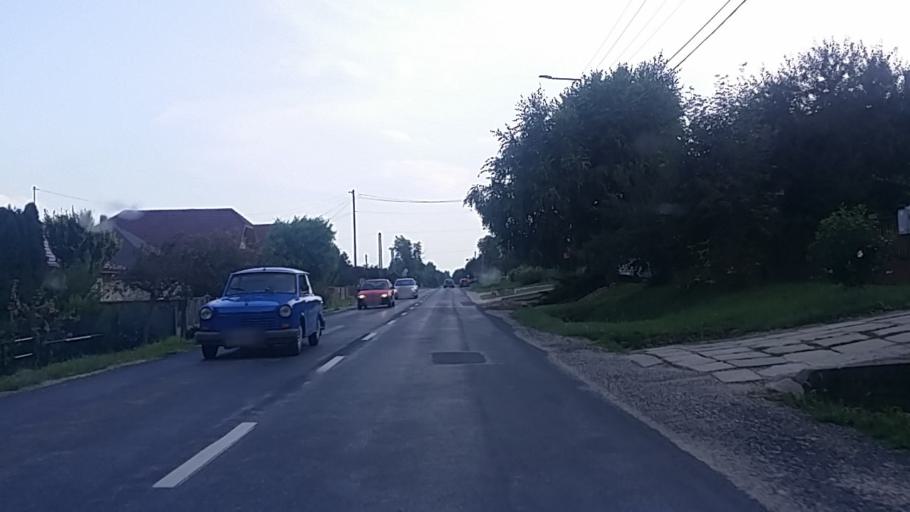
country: HU
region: Zala
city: Heviz
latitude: 46.7563
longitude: 17.1749
